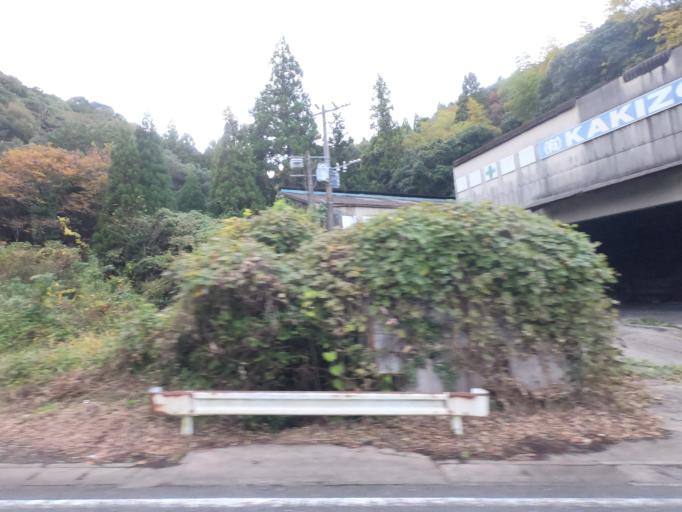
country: JP
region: Kumamoto
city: Minamata
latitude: 32.2550
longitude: 130.5060
